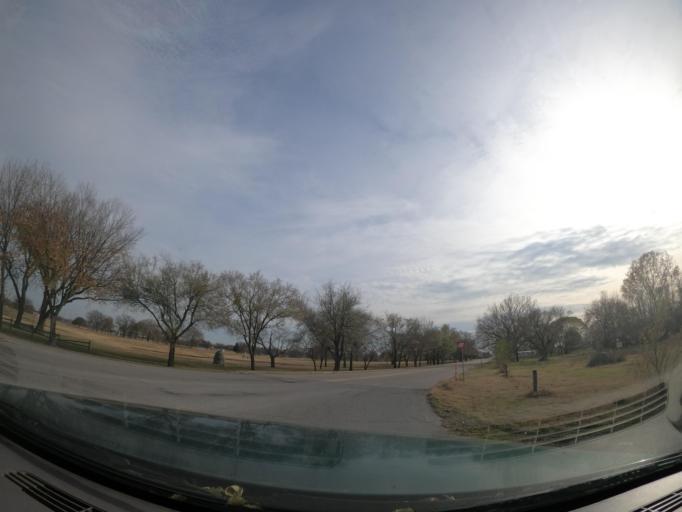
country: US
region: Oklahoma
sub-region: Tulsa County
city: Turley
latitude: 36.2493
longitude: -95.9585
